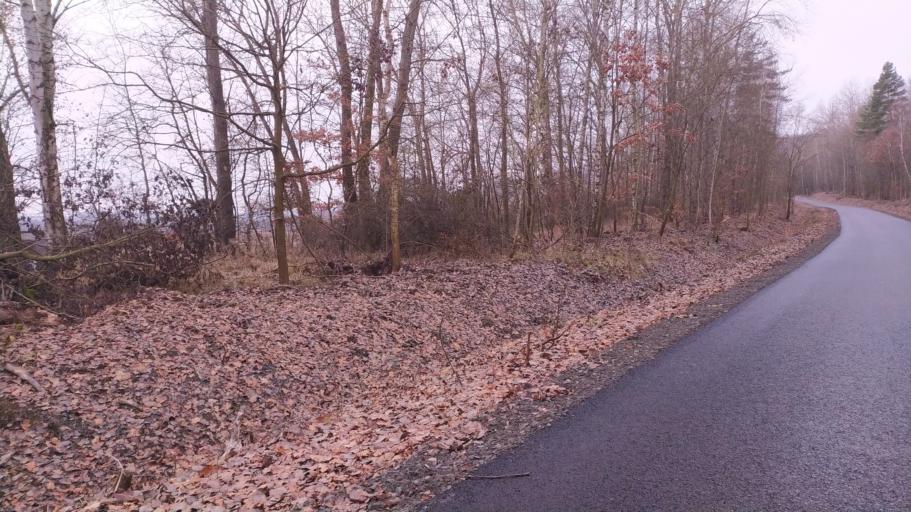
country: DE
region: Bavaria
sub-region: Upper Franconia
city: Schirnding
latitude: 50.1035
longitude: 12.2626
